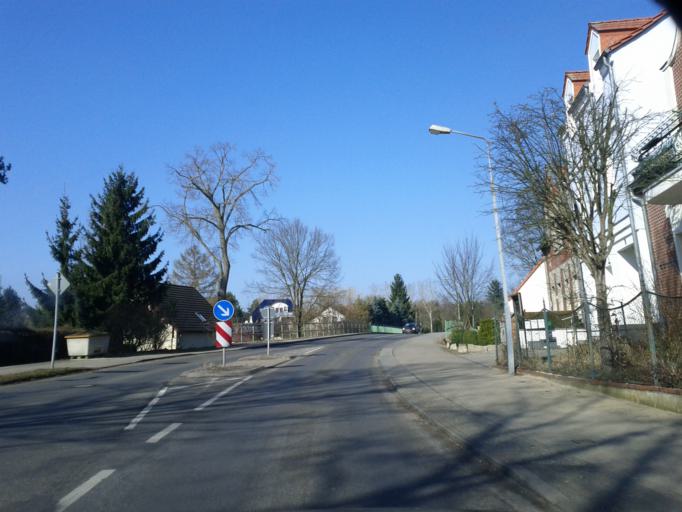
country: DE
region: Brandenburg
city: Grunheide
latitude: 52.4196
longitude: 13.7988
